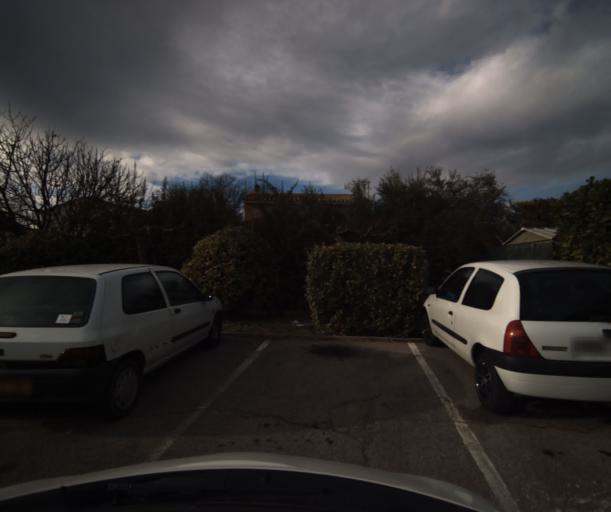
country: FR
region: Provence-Alpes-Cote d'Azur
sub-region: Departement du Vaucluse
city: Pertuis
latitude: 43.6902
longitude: 5.5245
